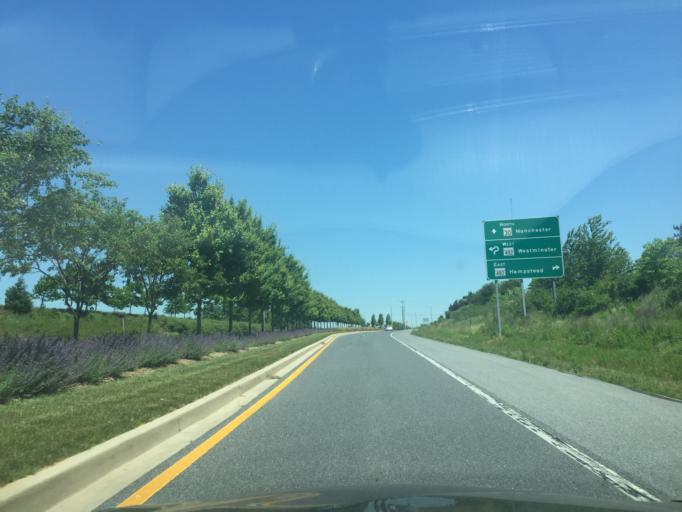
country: US
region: Maryland
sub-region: Carroll County
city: Hampstead
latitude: 39.6081
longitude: -76.8657
